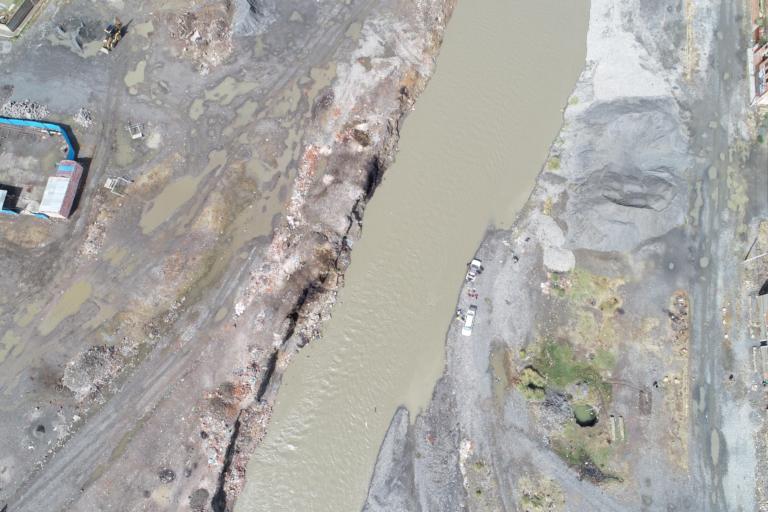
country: BO
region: La Paz
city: Achacachi
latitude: -16.0385
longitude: -68.6874
